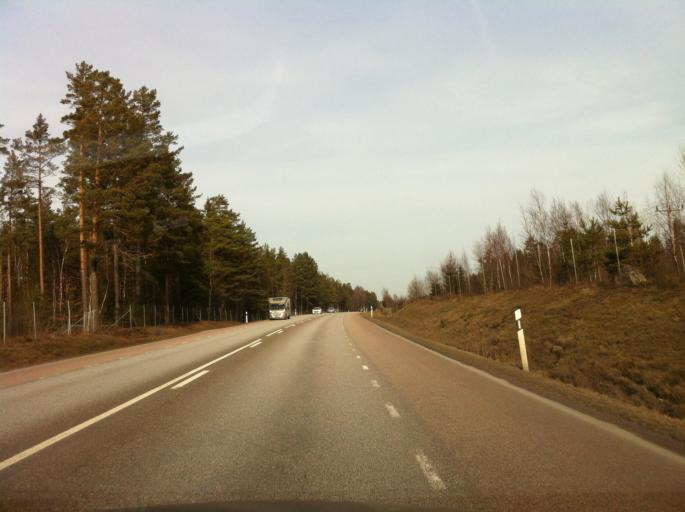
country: SE
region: Vaestra Goetaland
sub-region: Mariestads Kommun
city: Mariestad
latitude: 58.6969
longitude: 13.8625
